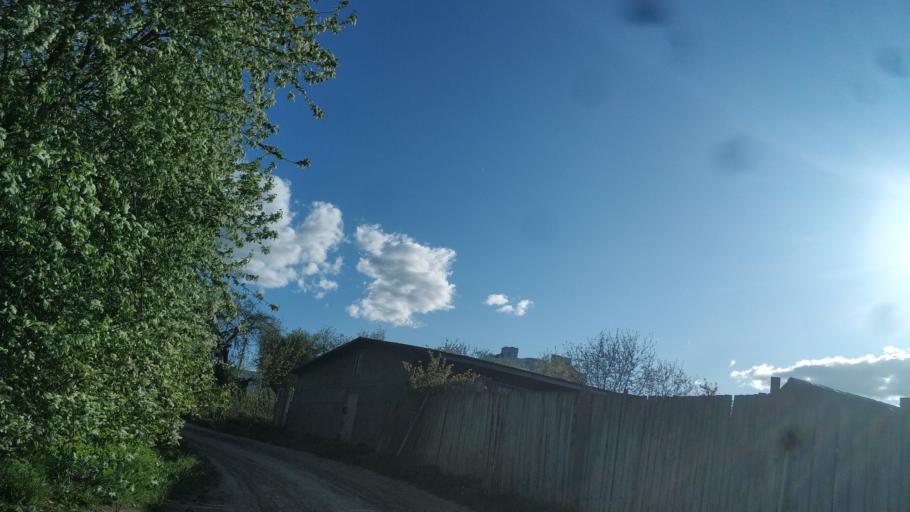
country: BY
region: Minsk
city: Syenitsa
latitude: 53.8471
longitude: 27.5739
